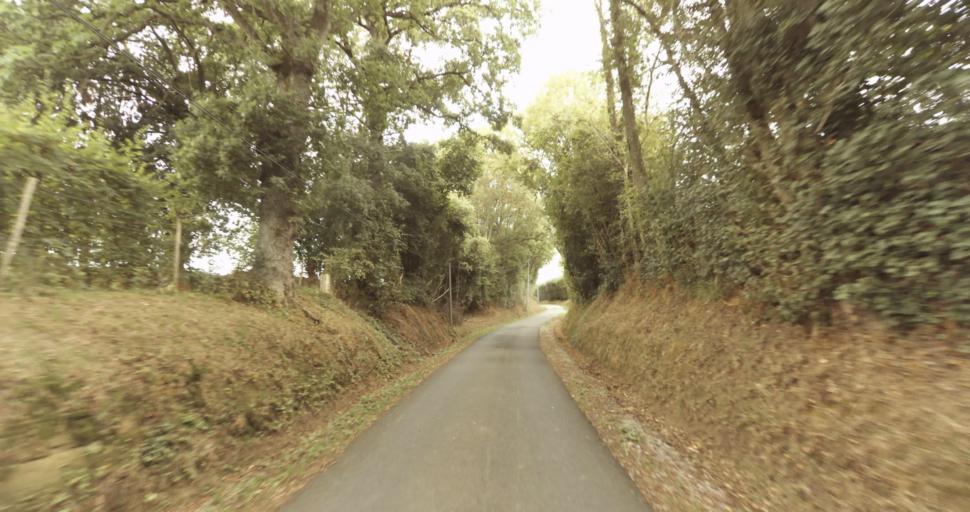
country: FR
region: Lower Normandy
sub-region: Departement de l'Orne
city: Sees
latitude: 48.6740
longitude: 0.2619
